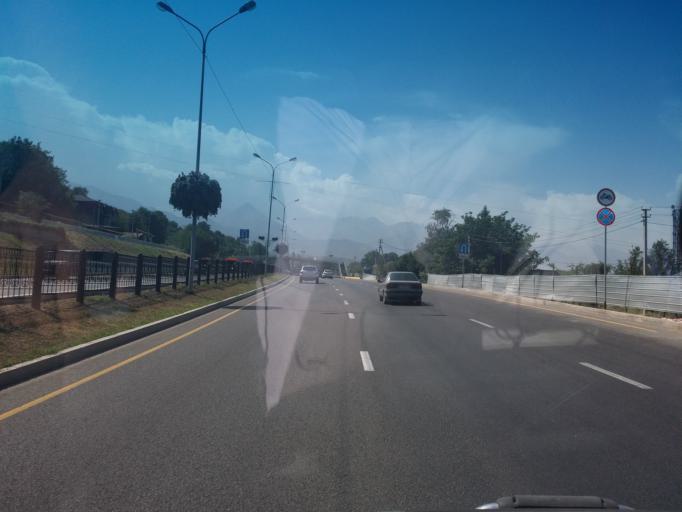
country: KZ
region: Almaty Qalasy
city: Almaty
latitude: 43.2364
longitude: 76.9702
